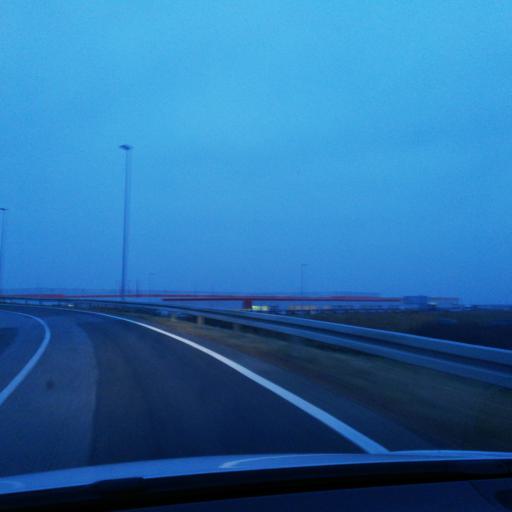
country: RS
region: Autonomna Pokrajina Vojvodina
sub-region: Sremski Okrug
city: Ruma
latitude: 44.9603
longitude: 19.8097
